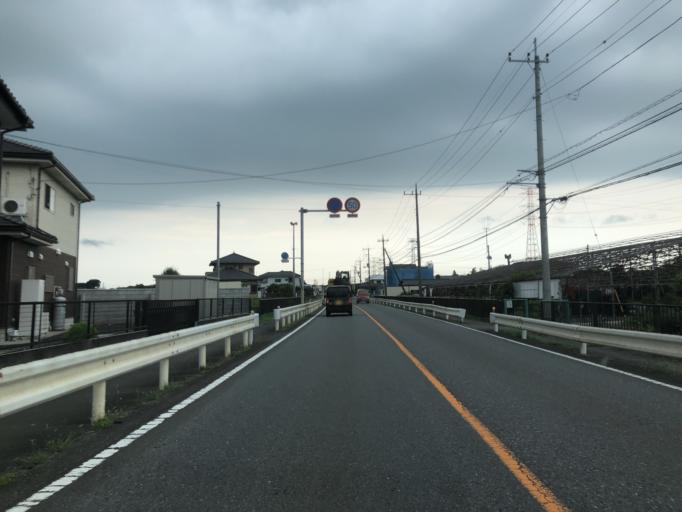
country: JP
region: Saitama
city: Sakado
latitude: 36.0228
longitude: 139.3960
